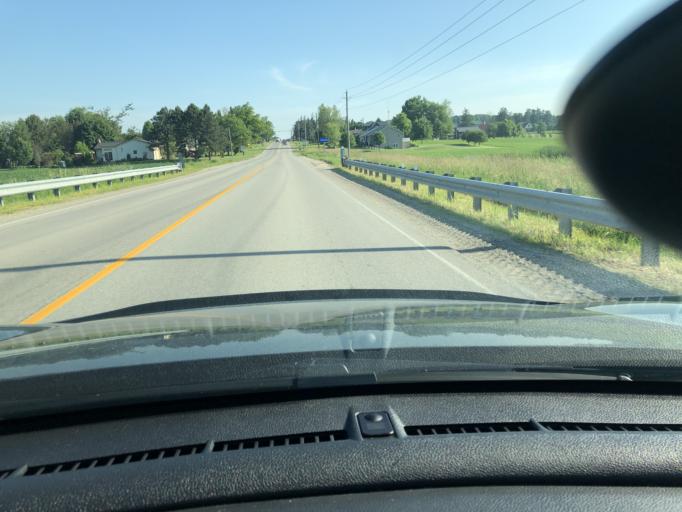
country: CA
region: Ontario
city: Stratford
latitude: 43.4219
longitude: -80.8381
